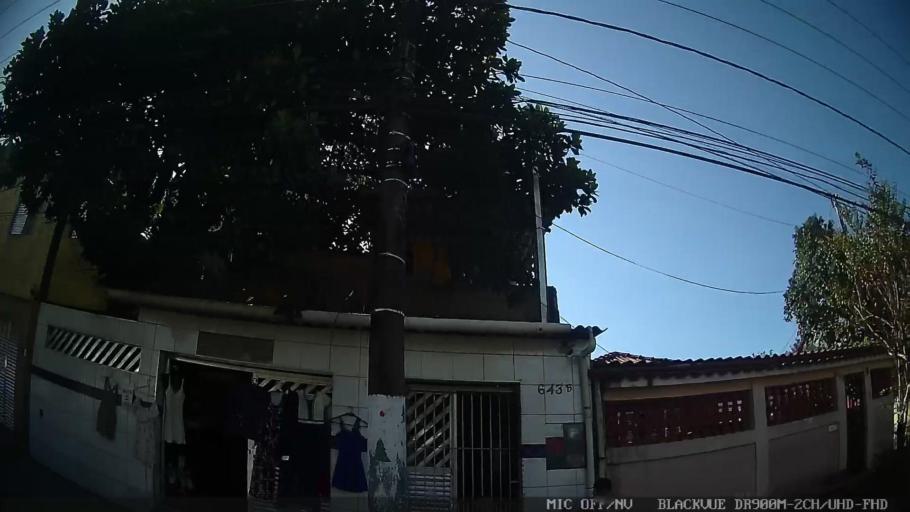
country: BR
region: Sao Paulo
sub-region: Santos
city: Santos
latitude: -23.9514
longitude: -46.2872
